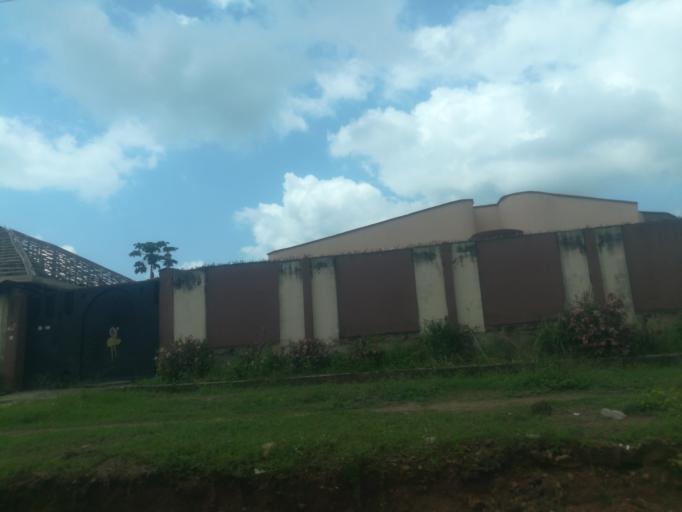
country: NG
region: Oyo
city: Ibadan
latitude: 7.3591
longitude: 3.8419
